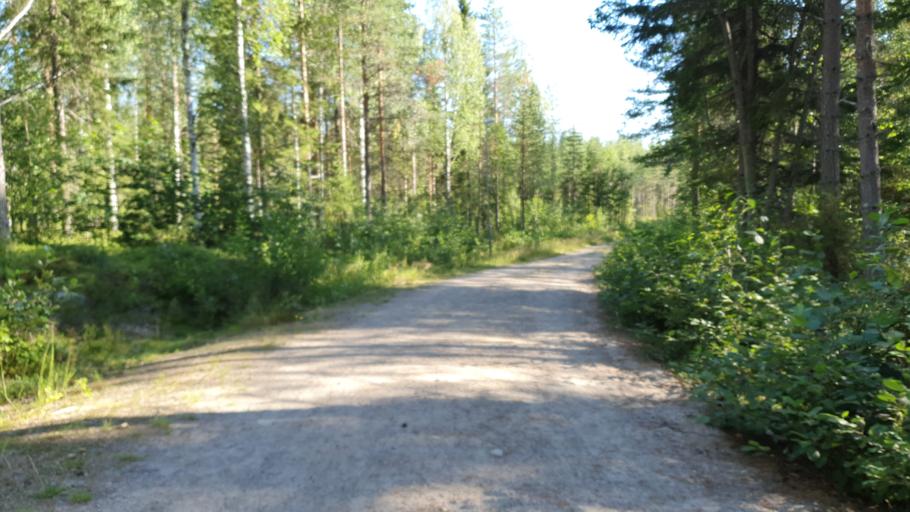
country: FI
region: Kainuu
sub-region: Kehys-Kainuu
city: Kuhmo
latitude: 64.1123
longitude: 29.5053
